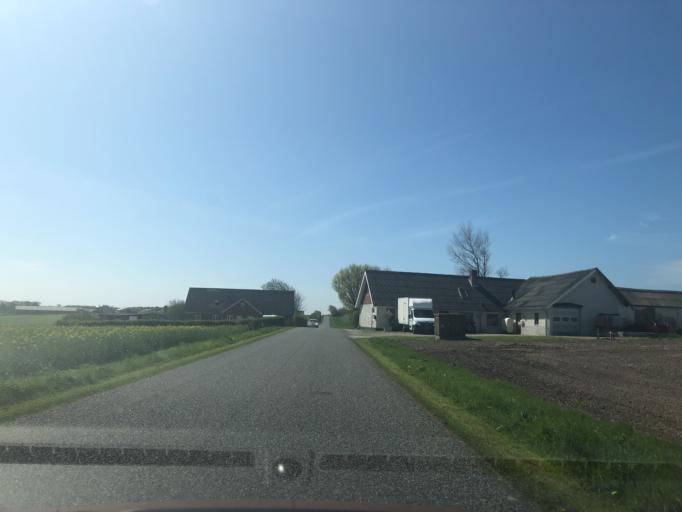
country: DK
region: Central Jutland
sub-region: Holstebro Kommune
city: Vinderup
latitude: 56.5829
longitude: 8.7728
